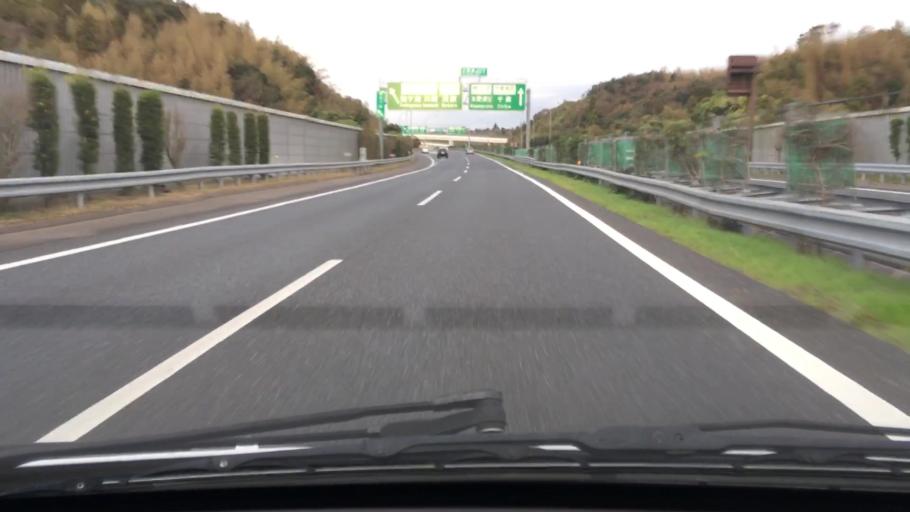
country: JP
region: Chiba
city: Kisarazu
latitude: 35.3712
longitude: 139.9725
